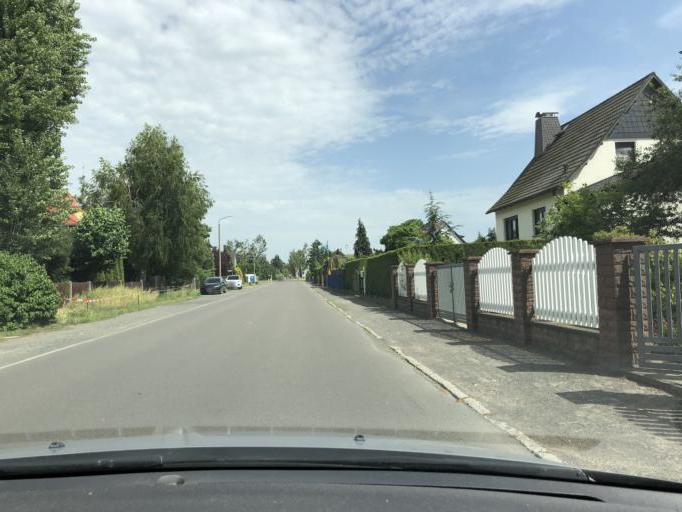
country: DE
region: Saxony
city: Taucha
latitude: 51.3702
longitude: 12.5084
